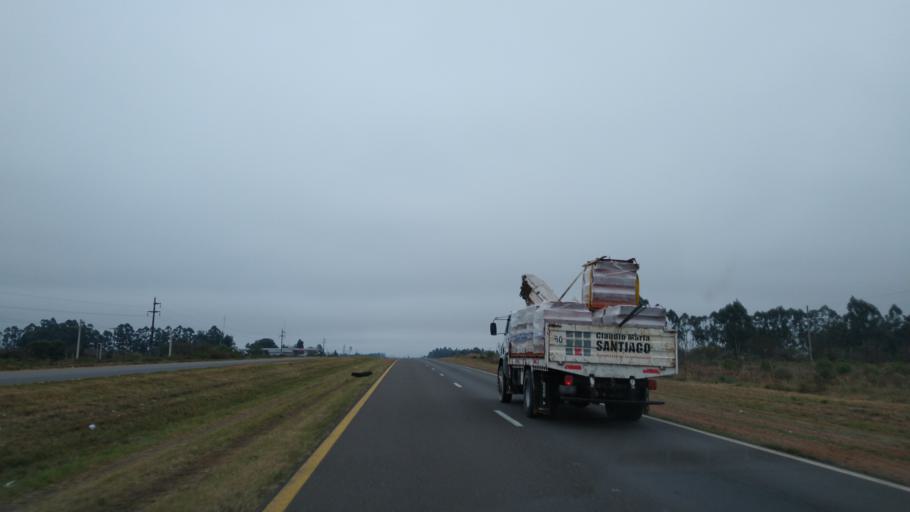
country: AR
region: Entre Rios
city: Chajari
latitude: -30.8222
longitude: -58.0453
